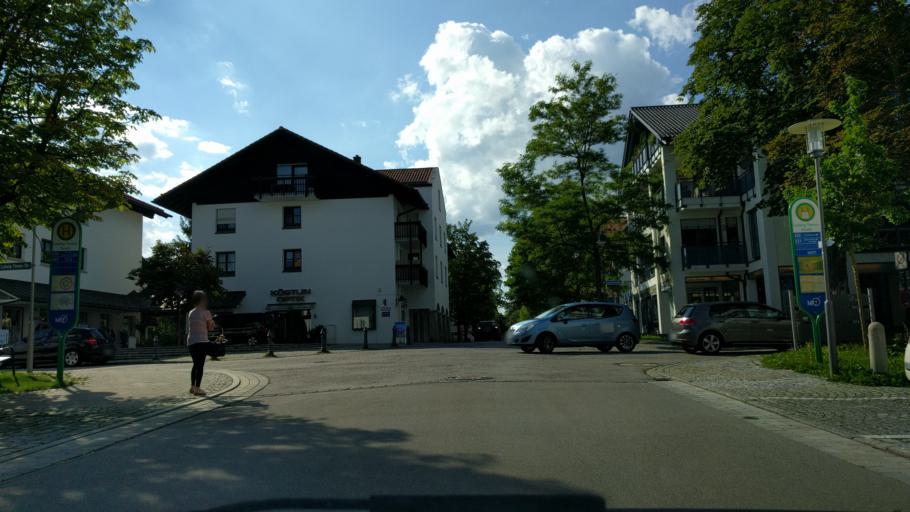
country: DE
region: Bavaria
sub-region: Upper Bavaria
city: Oberhaching
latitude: 48.0192
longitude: 11.5874
